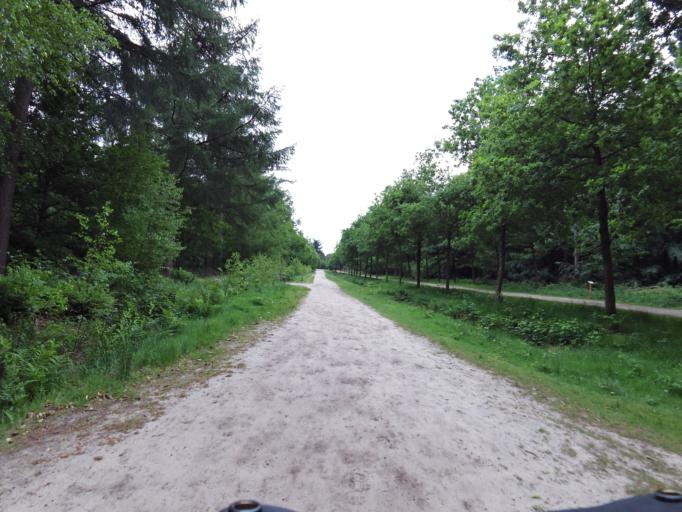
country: NL
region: North Brabant
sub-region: Gemeente Breda
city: Breda
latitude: 51.5608
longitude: 4.7762
